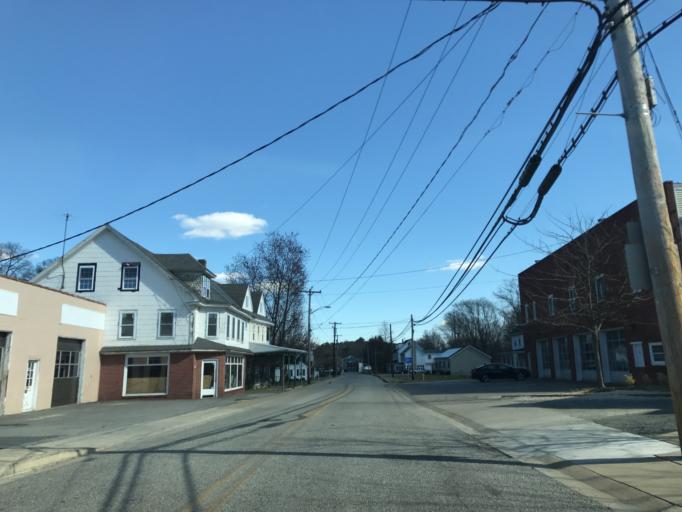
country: US
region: Maryland
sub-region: Kent County
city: Rock Hall
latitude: 39.1366
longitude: -76.2346
